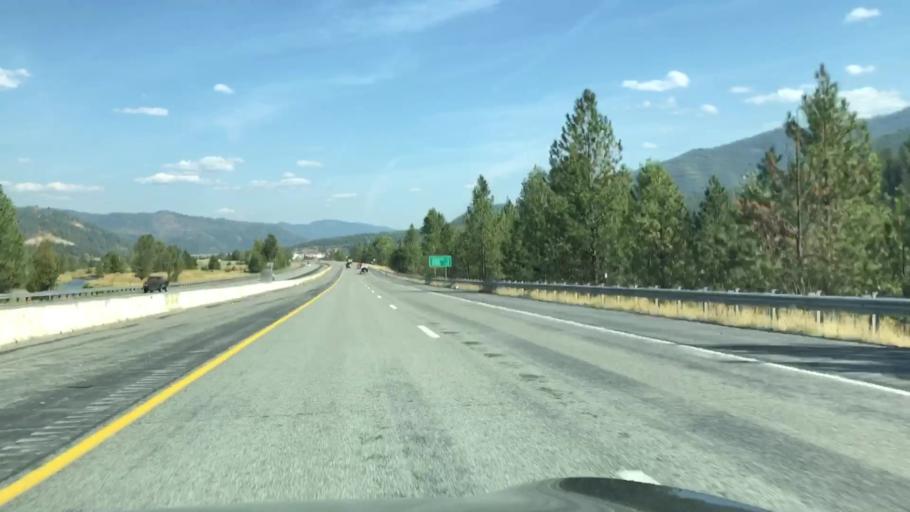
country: US
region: Idaho
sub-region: Shoshone County
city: Pinehurst
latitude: 47.5474
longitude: -116.2162
